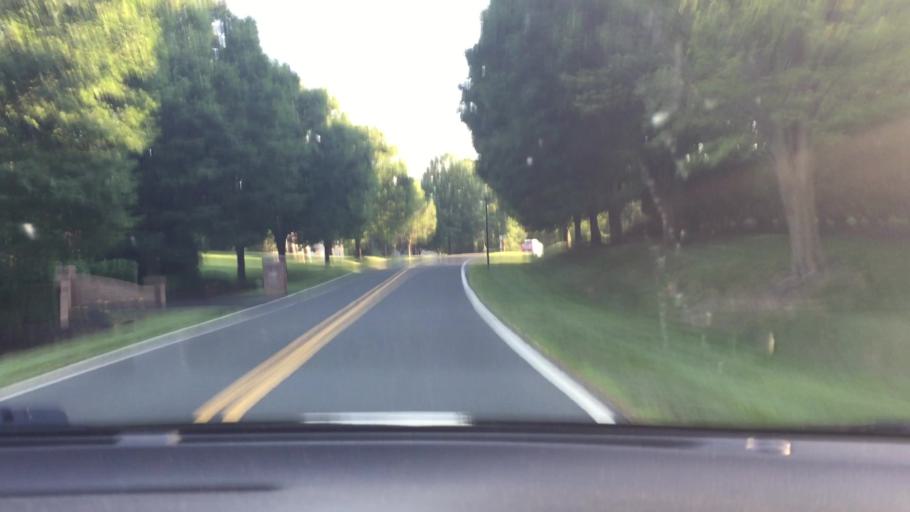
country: US
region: Maryland
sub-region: Montgomery County
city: Potomac
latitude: 39.0180
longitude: -77.1826
